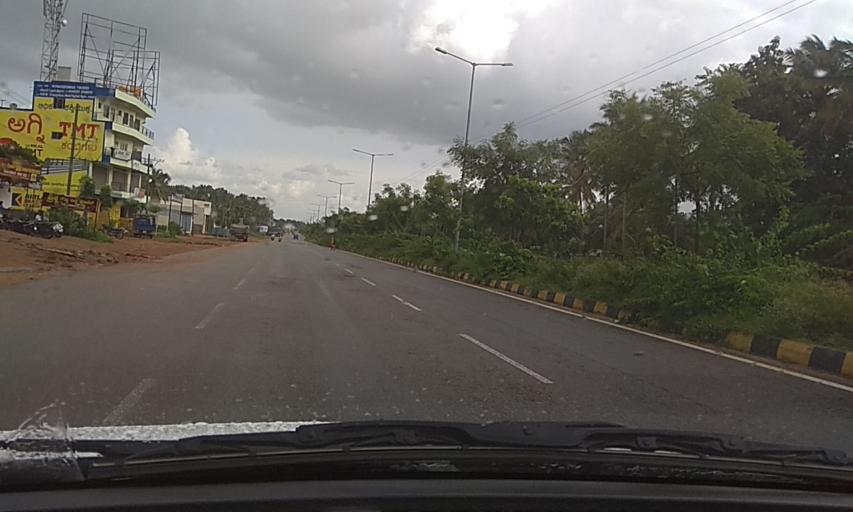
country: IN
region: Karnataka
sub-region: Mysore
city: Mysore
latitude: 12.3030
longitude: 76.7042
